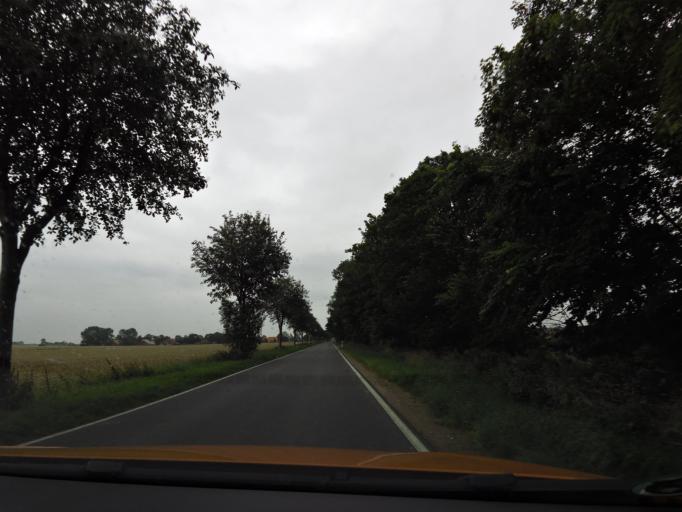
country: DE
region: Lower Saxony
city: Wirdum
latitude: 53.5090
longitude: 7.1488
